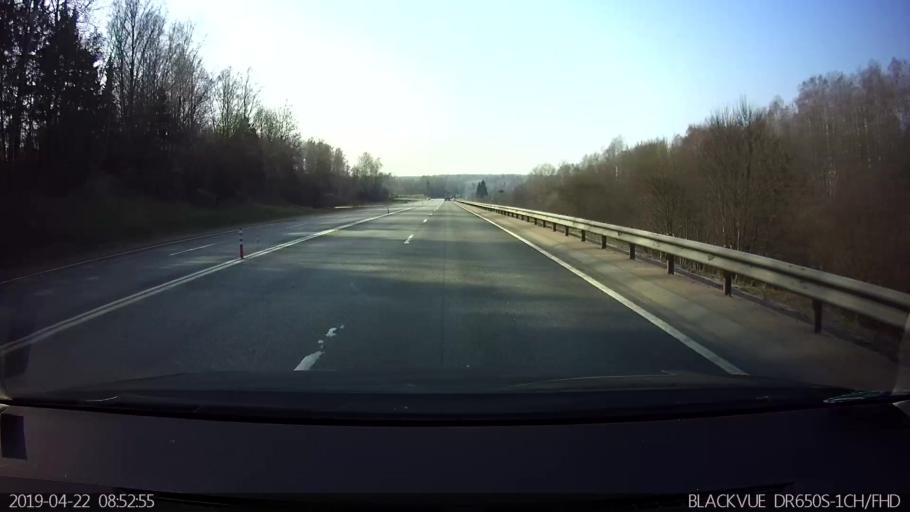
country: RU
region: Smolensk
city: Pechersk
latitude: 54.9019
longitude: 32.1207
